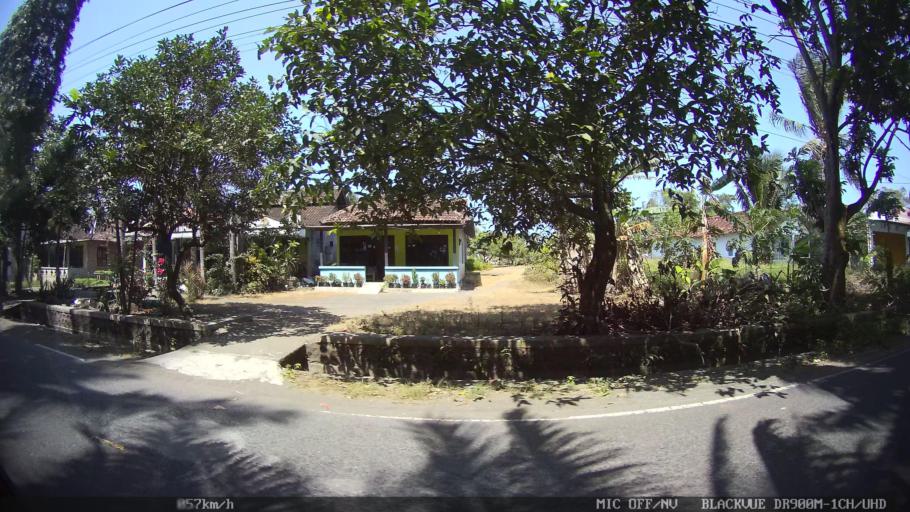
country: ID
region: Daerah Istimewa Yogyakarta
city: Srandakan
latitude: -7.9166
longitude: 110.1035
